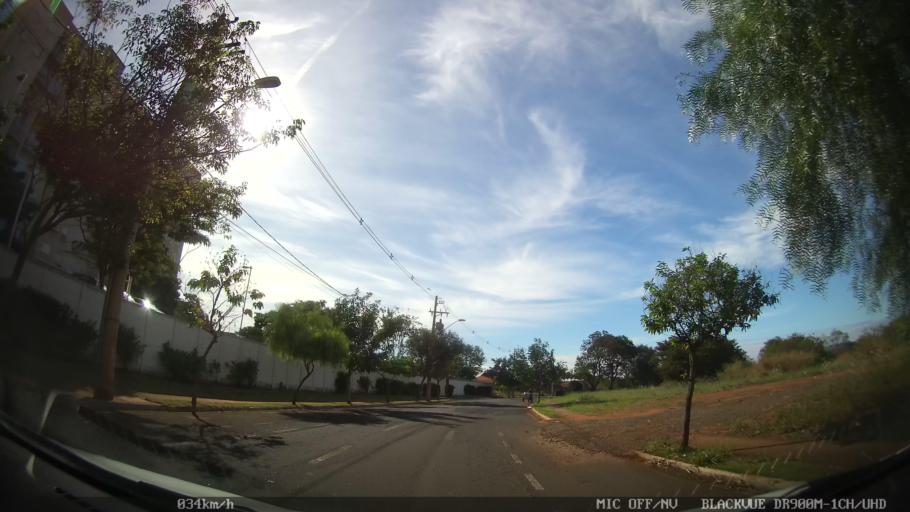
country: BR
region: Sao Paulo
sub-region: Sao Jose Do Rio Preto
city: Sao Jose do Rio Preto
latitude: -20.7862
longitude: -49.3502
